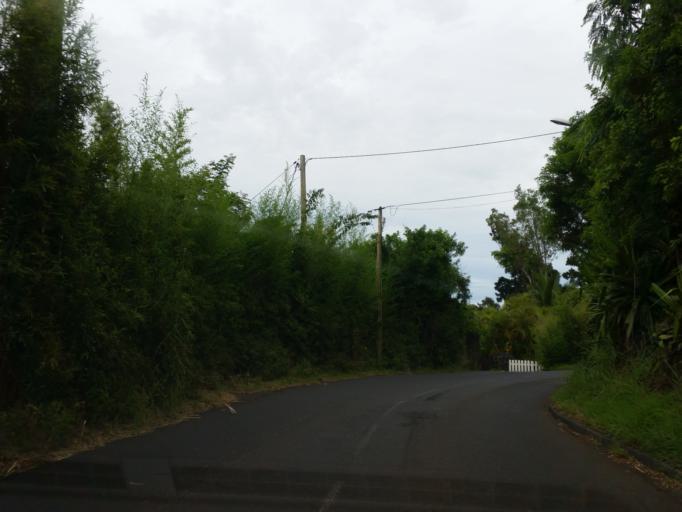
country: RE
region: Reunion
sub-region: Reunion
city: Saint-Denis
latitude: -20.8827
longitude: 55.4313
